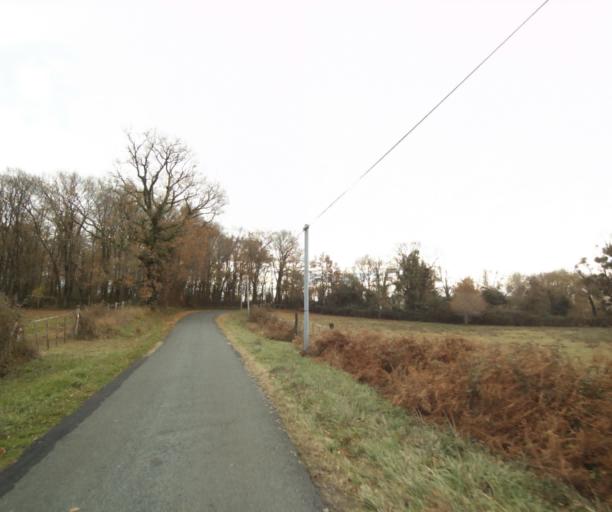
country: FR
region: Poitou-Charentes
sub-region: Departement de la Charente-Maritime
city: Corme-Royal
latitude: 45.7335
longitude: -0.7808
